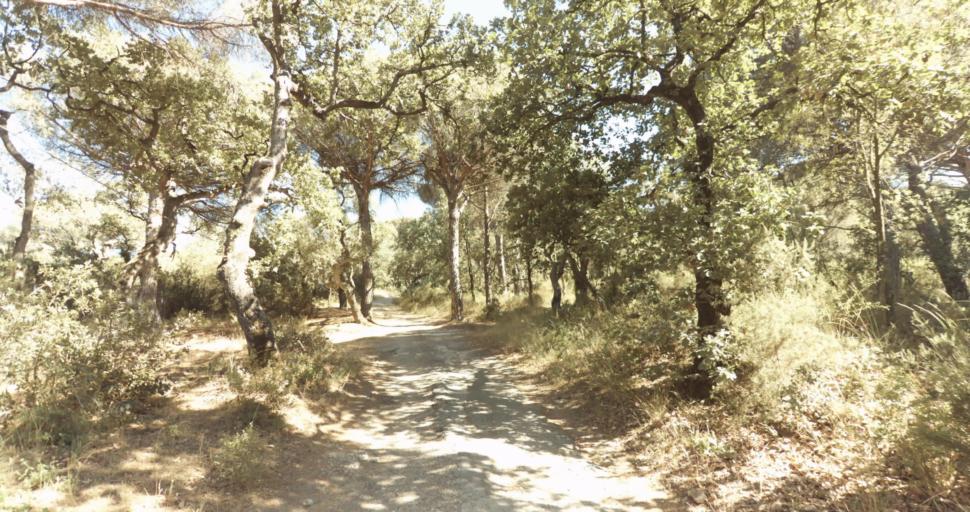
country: FR
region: Provence-Alpes-Cote d'Azur
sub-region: Departement du Var
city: Gassin
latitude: 43.2531
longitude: 6.5862
